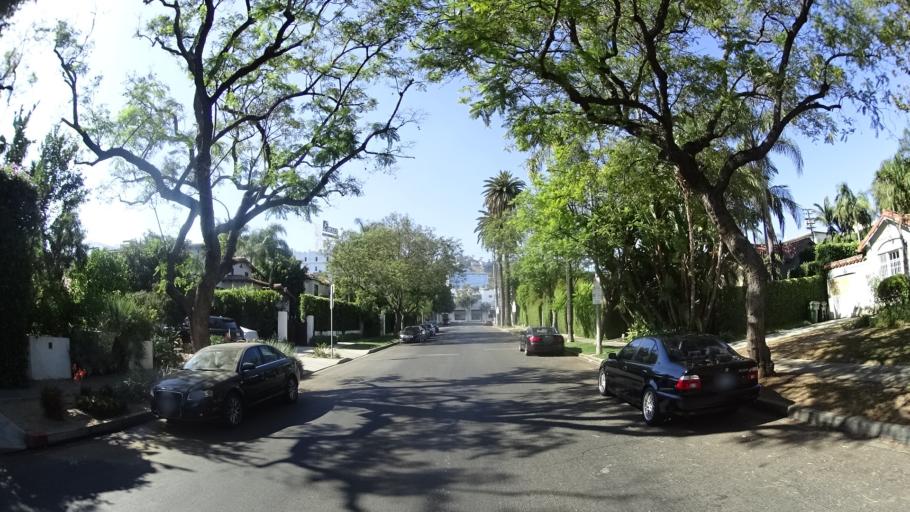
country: US
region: California
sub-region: Los Angeles County
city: West Hollywood
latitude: 34.0894
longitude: -118.3731
